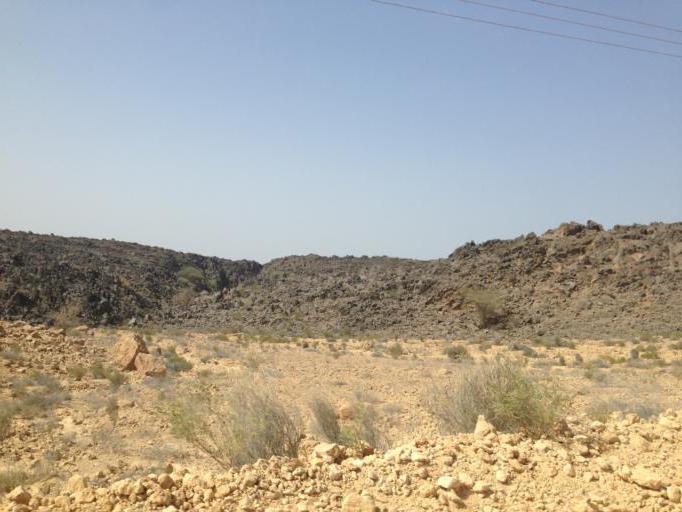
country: OM
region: Ash Sharqiyah
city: Ibra'
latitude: 23.0849
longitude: 58.9391
